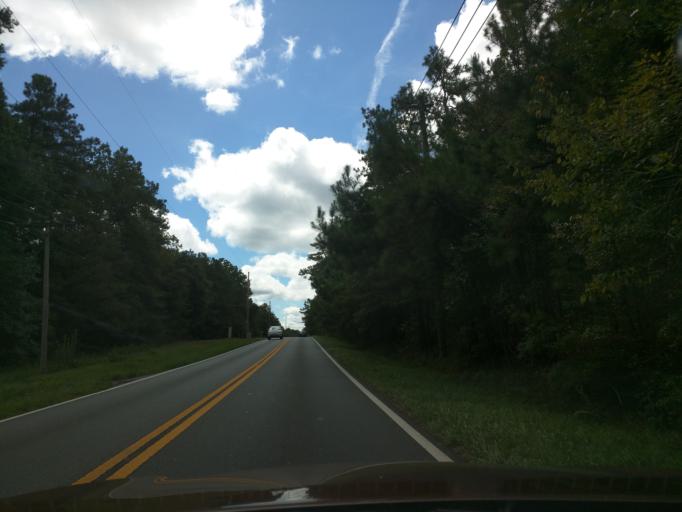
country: US
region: Florida
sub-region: Leon County
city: Tallahassee
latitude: 30.5746
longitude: -84.2308
